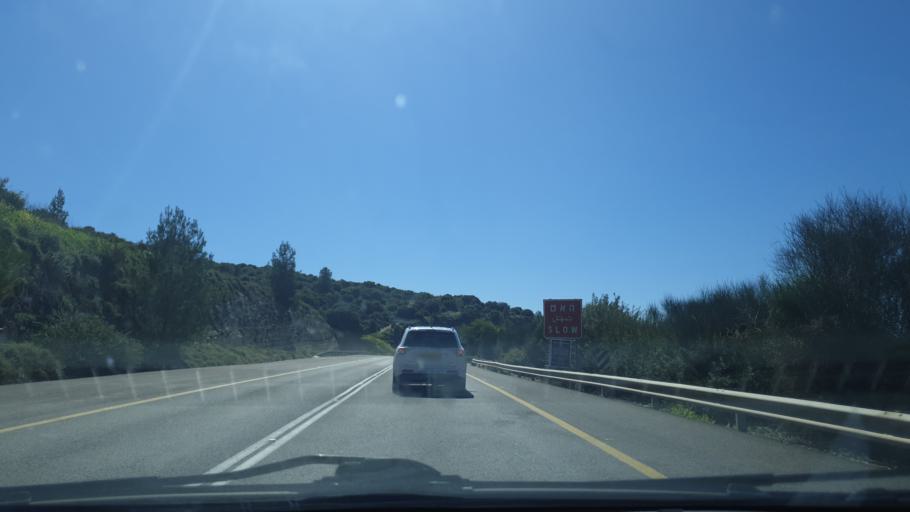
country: IL
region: Jerusalem
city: Bet Shemesh
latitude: 31.6962
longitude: 34.9427
